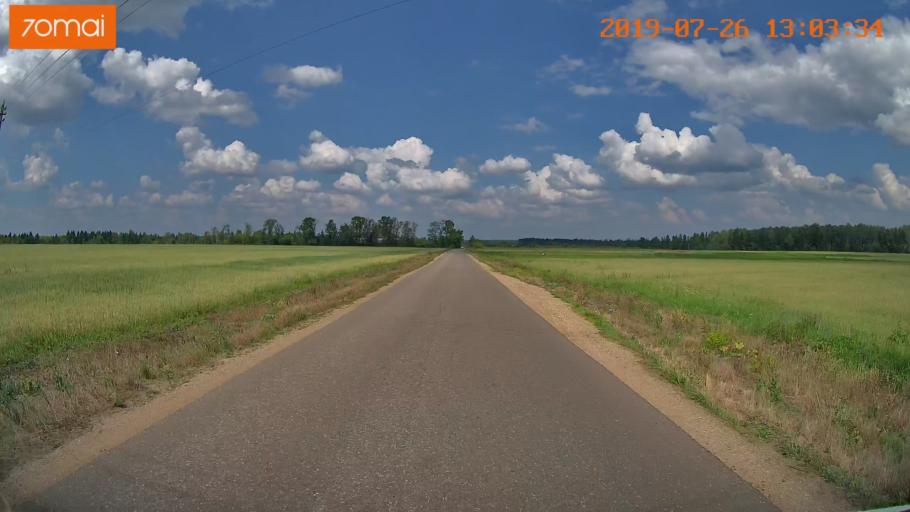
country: RU
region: Ivanovo
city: Bogorodskoye
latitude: 57.0470
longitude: 41.0222
